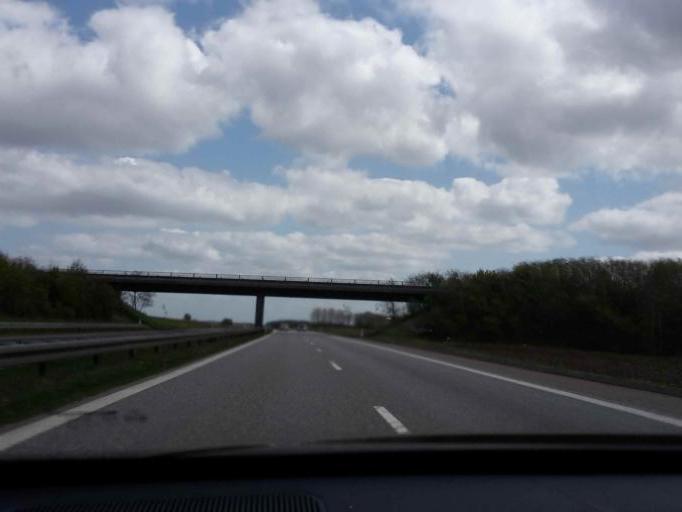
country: DK
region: South Denmark
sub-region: Esbjerg Kommune
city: Bramming
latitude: 55.5066
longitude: 8.6640
